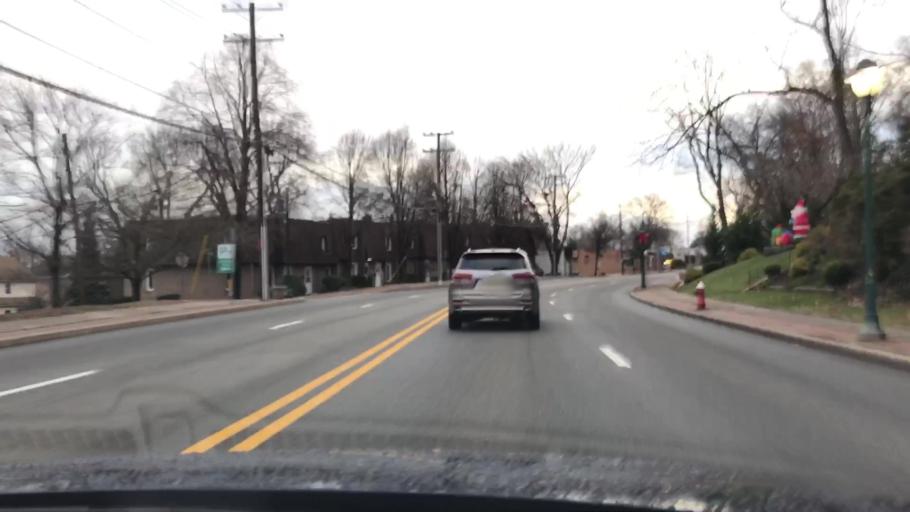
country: US
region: New Jersey
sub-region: Bergen County
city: New Milford
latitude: 40.9454
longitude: -74.0287
